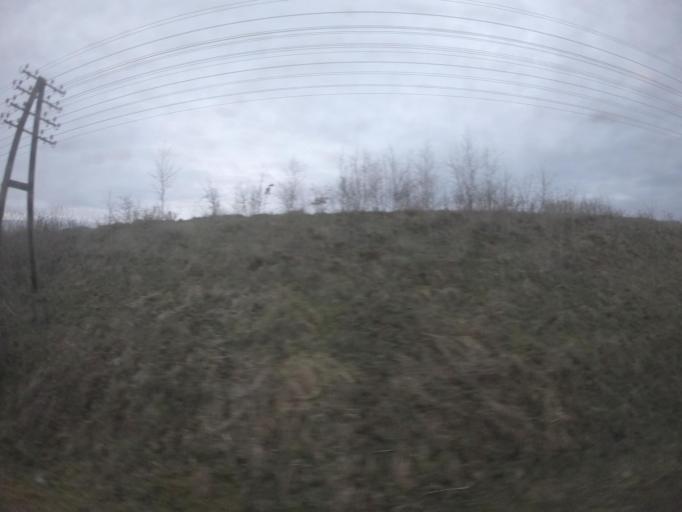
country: PL
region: West Pomeranian Voivodeship
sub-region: Powiat szczecinecki
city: Lubowo
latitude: 53.6225
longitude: 16.4551
